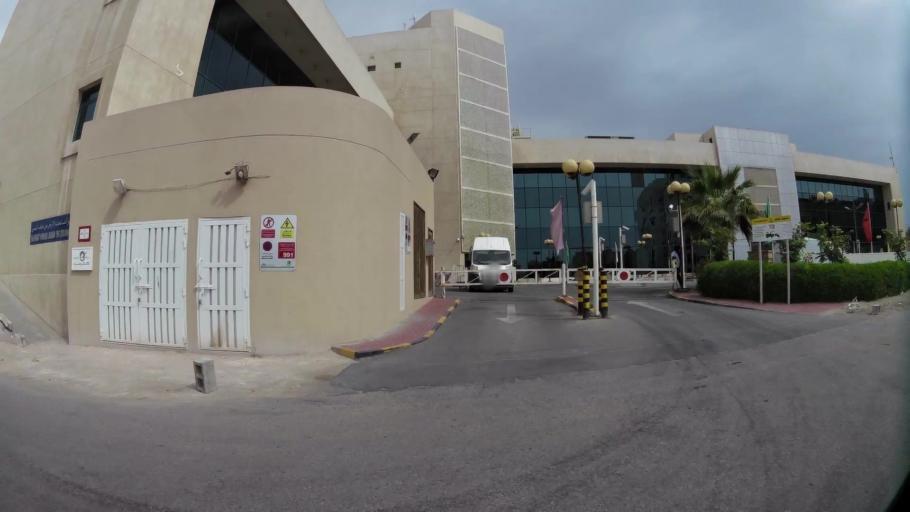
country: QA
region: Baladiyat ad Dawhah
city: Doha
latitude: 25.2905
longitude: 51.5022
